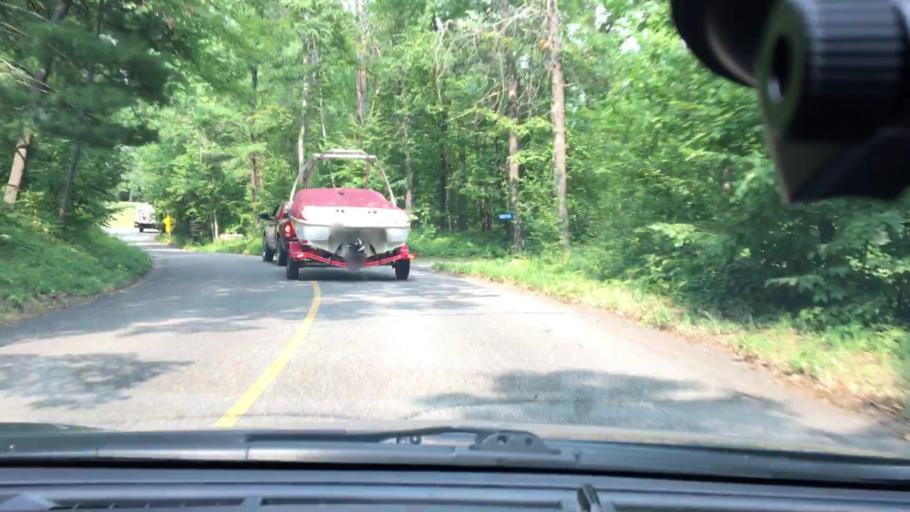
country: US
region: Minnesota
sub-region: Cass County
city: East Gull Lake
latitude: 46.4097
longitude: -94.3540
